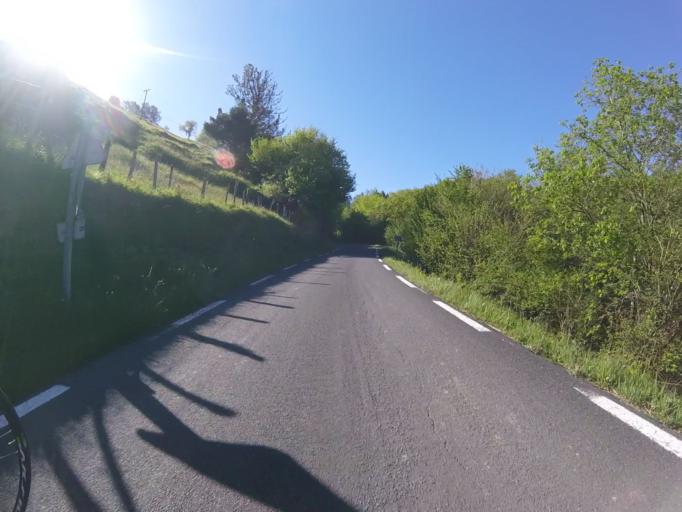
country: ES
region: Basque Country
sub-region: Provincia de Guipuzcoa
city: Aizarnazabal
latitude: 43.2197
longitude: -2.2125
